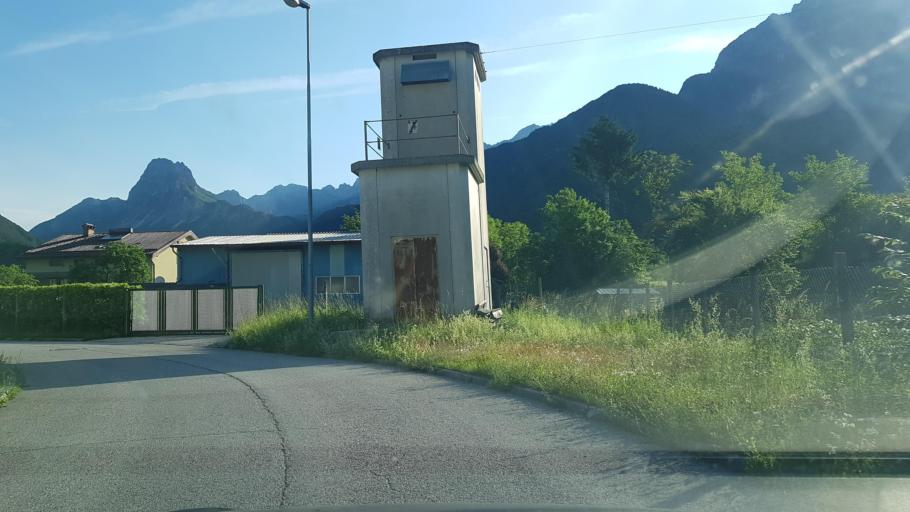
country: IT
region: Friuli Venezia Giulia
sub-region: Provincia di Udine
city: Moggio di Sotto
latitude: 46.4036
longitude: 13.1965
